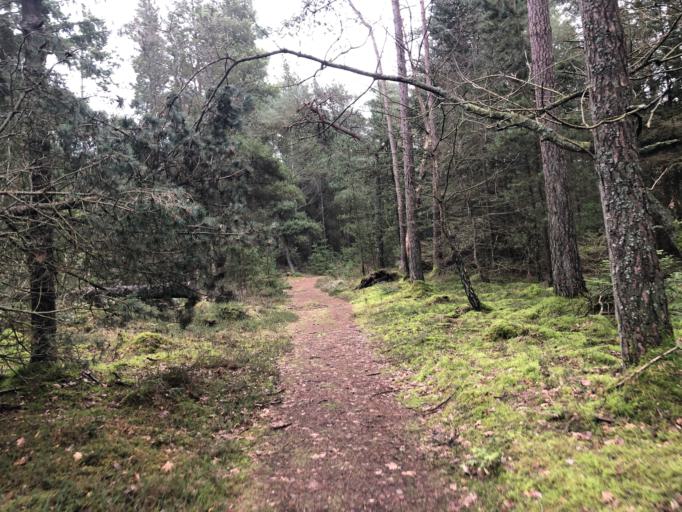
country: DK
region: Central Jutland
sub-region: Holstebro Kommune
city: Ulfborg
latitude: 56.2887
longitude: 8.1749
